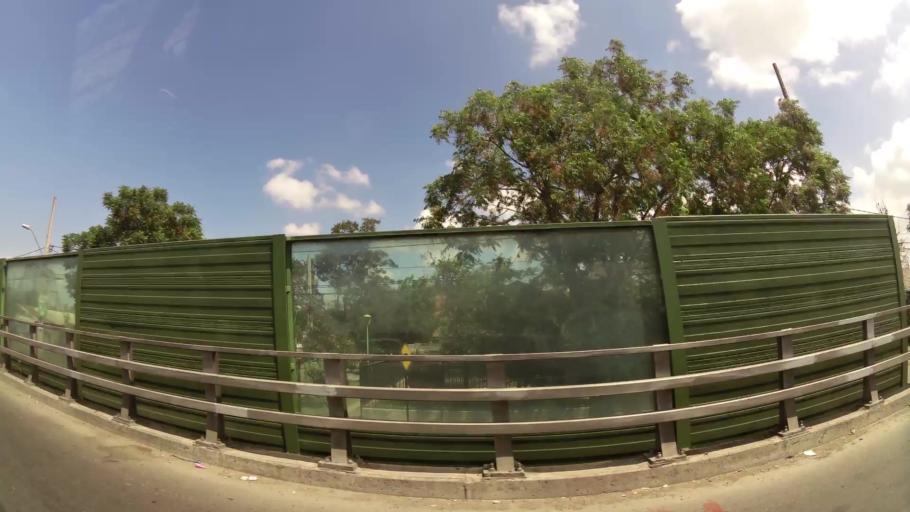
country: CL
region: Santiago Metropolitan
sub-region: Provincia de Santiago
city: Lo Prado
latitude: -33.5121
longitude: -70.7171
